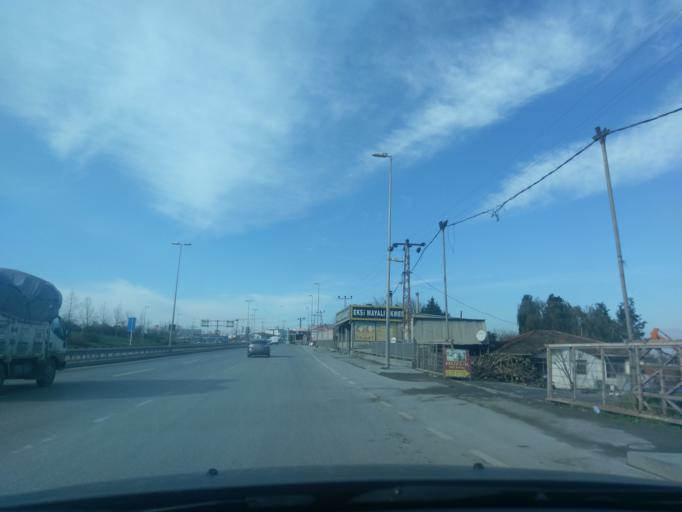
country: TR
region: Istanbul
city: Basaksehir
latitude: 41.1360
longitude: 28.8225
